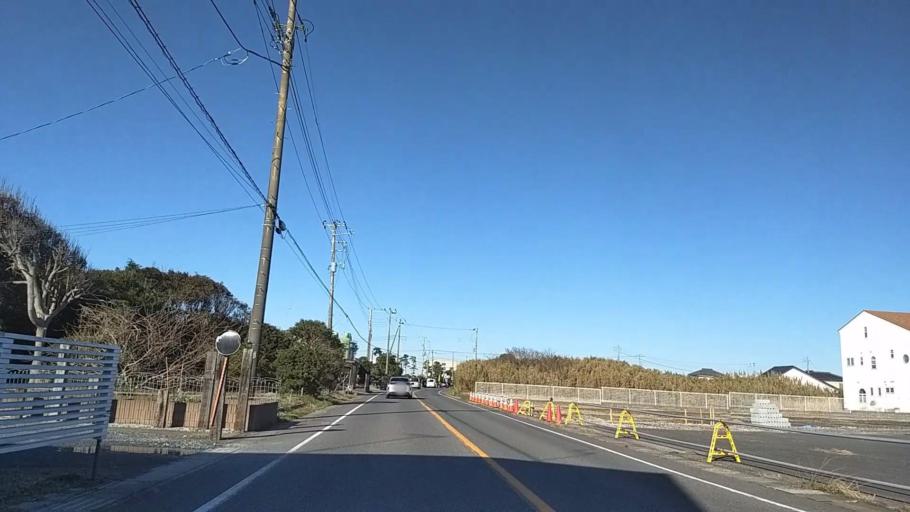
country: JP
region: Chiba
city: Mobara
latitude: 35.3763
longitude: 140.3875
